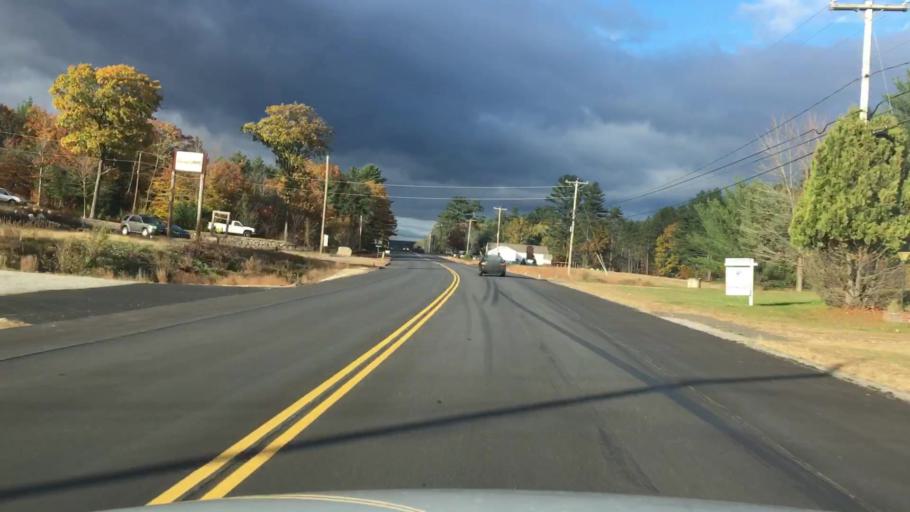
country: US
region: Maine
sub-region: Androscoggin County
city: Livermore
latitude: 44.3660
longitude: -70.2517
